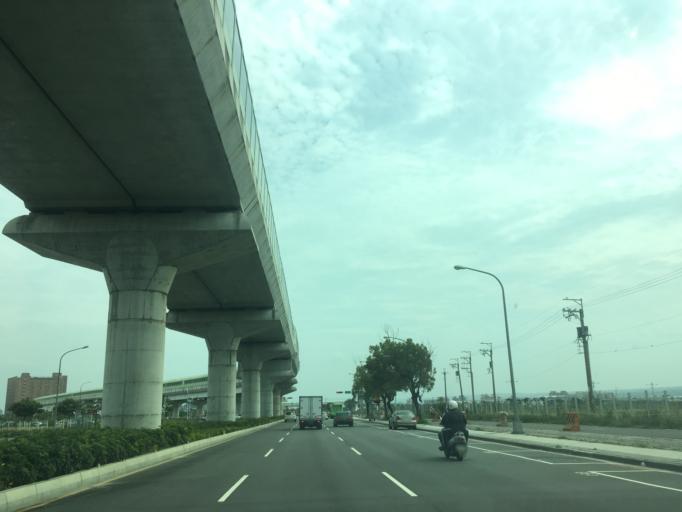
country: TW
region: Taiwan
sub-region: Taichung City
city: Taichung
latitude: 24.1277
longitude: 120.6463
